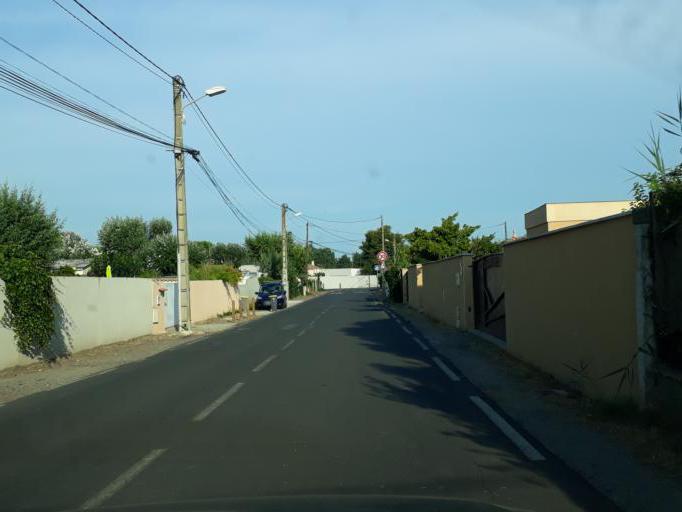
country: FR
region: Languedoc-Roussillon
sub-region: Departement de l'Herault
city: Agde
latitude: 43.2799
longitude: 3.4625
